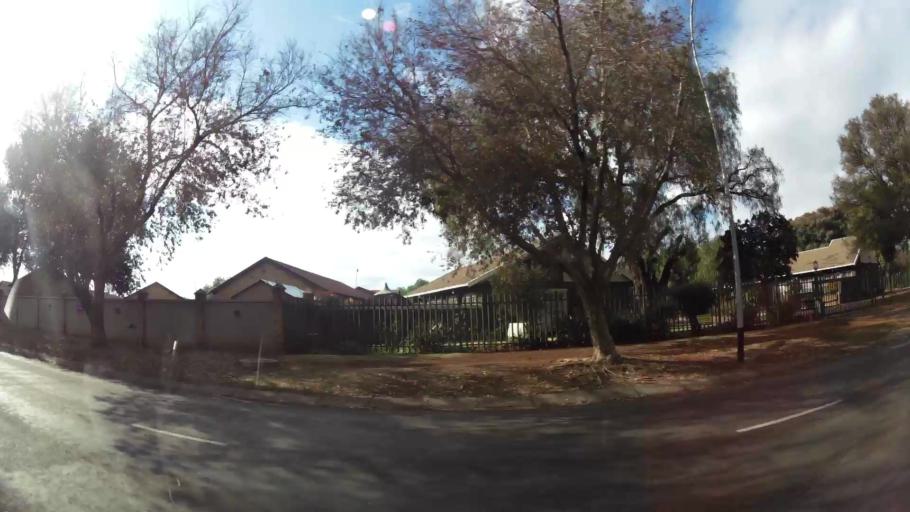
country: ZA
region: Gauteng
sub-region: Sedibeng District Municipality
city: Meyerton
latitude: -26.5516
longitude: 28.0331
